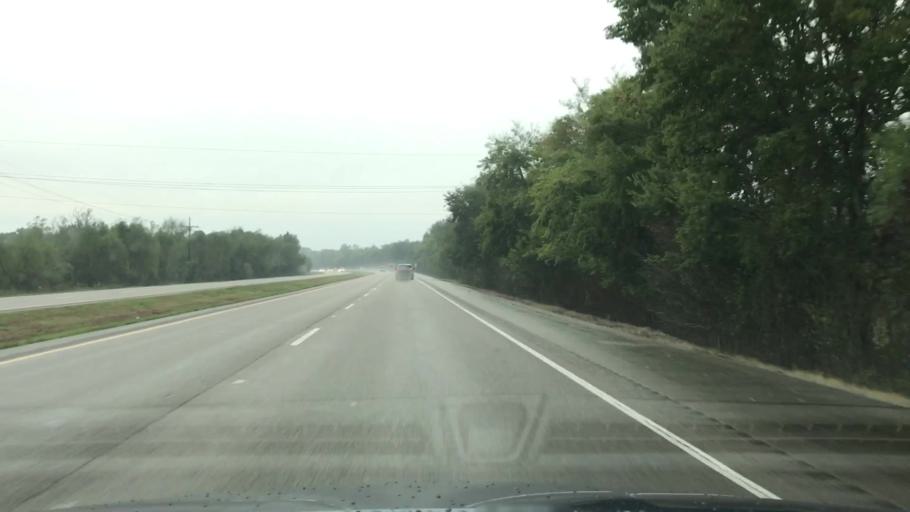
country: US
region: Louisiana
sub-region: Saint Charles Parish
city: Paradis
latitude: 29.8584
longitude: -90.4471
